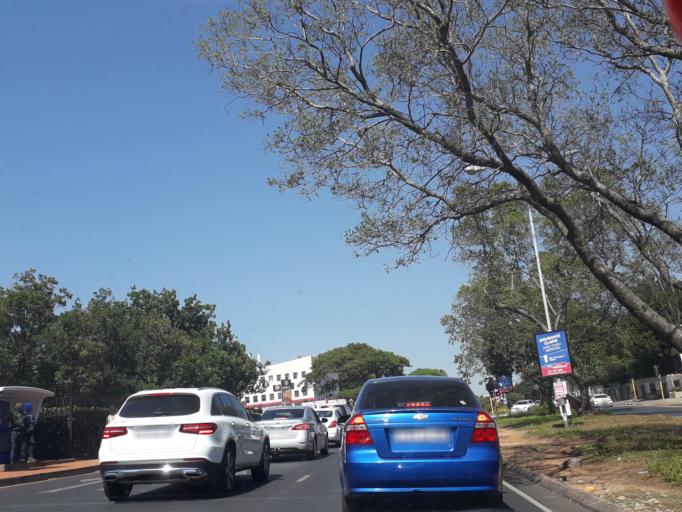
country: ZA
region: Gauteng
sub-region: City of Johannesburg Metropolitan Municipality
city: Johannesburg
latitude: -26.1144
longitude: 28.0504
